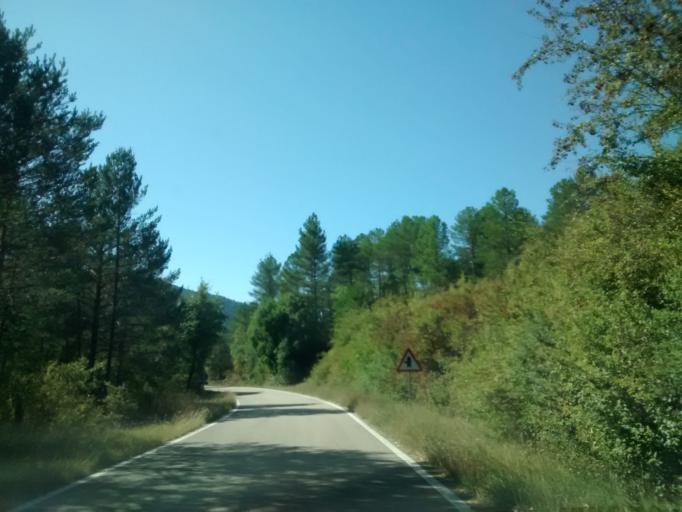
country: ES
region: Aragon
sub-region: Provincia de Huesca
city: Santa Cruz de la Seros
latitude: 42.4325
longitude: -0.6230
